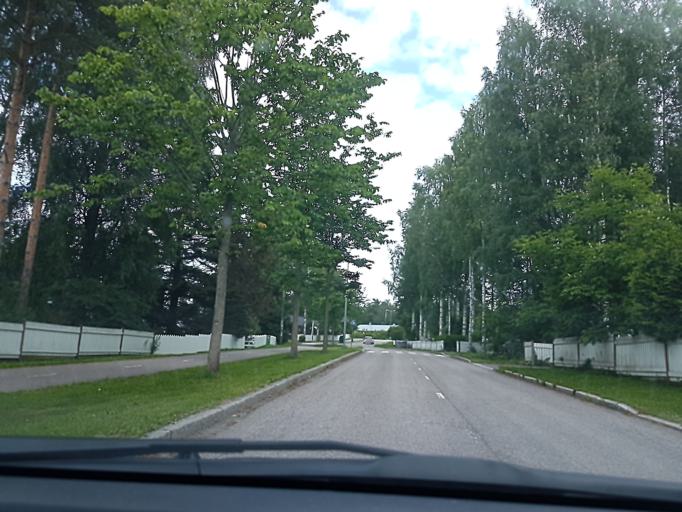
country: FI
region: Uusimaa
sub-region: Helsinki
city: Jaervenpaeae
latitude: 60.5059
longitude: 25.0954
